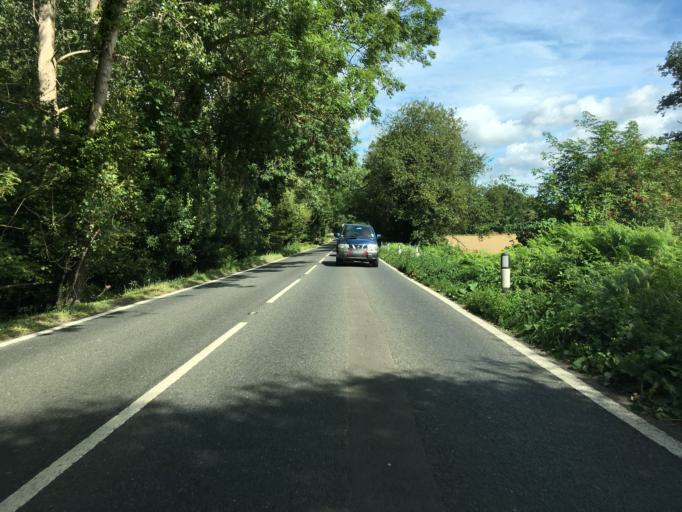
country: GB
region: England
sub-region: Kent
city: Staplehurst
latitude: 51.1308
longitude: 0.5601
